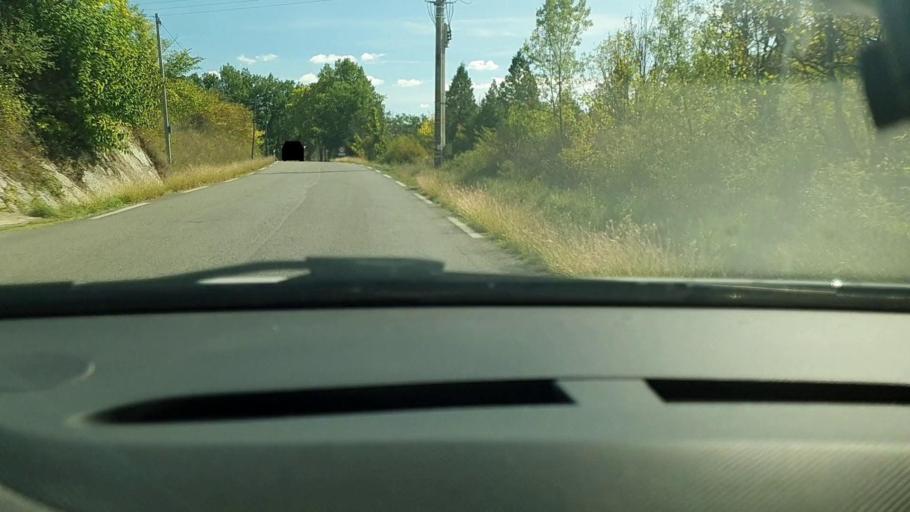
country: FR
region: Languedoc-Roussillon
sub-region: Departement du Gard
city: Saint-Ambroix
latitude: 44.2485
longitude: 4.2136
